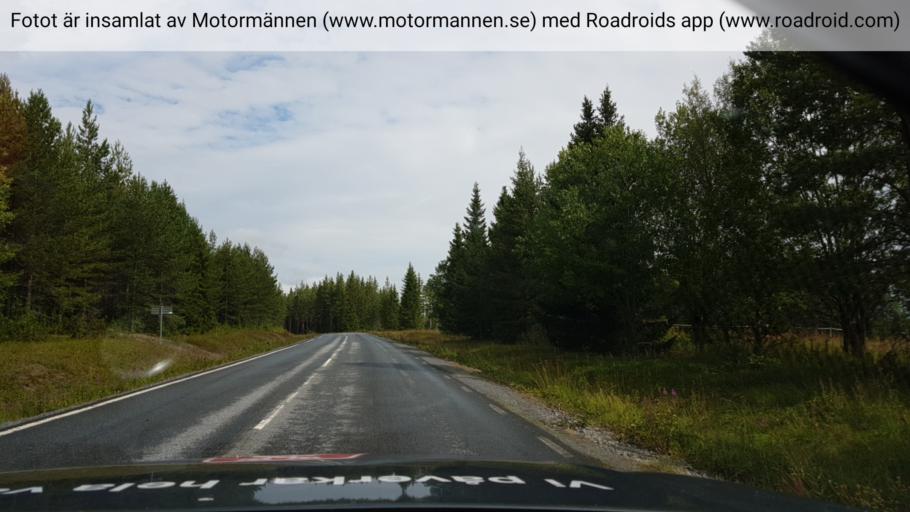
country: SE
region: Jaemtland
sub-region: Krokoms Kommun
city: Krokom
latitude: 63.2494
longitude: 14.4249
